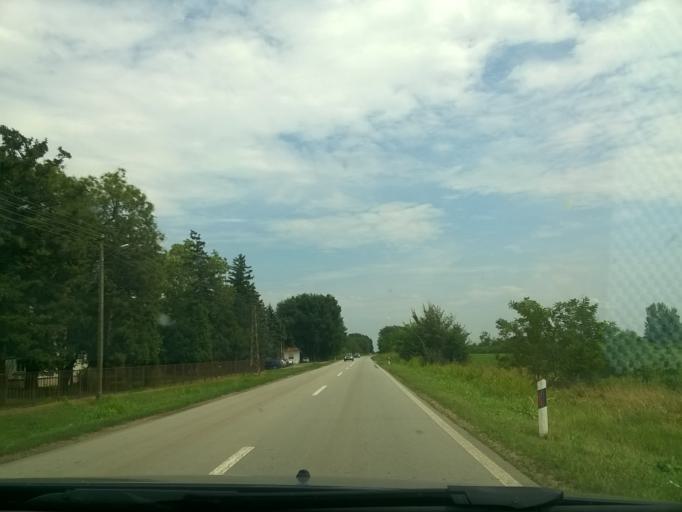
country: RS
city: Velika Greda
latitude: 45.2478
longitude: 21.0561
